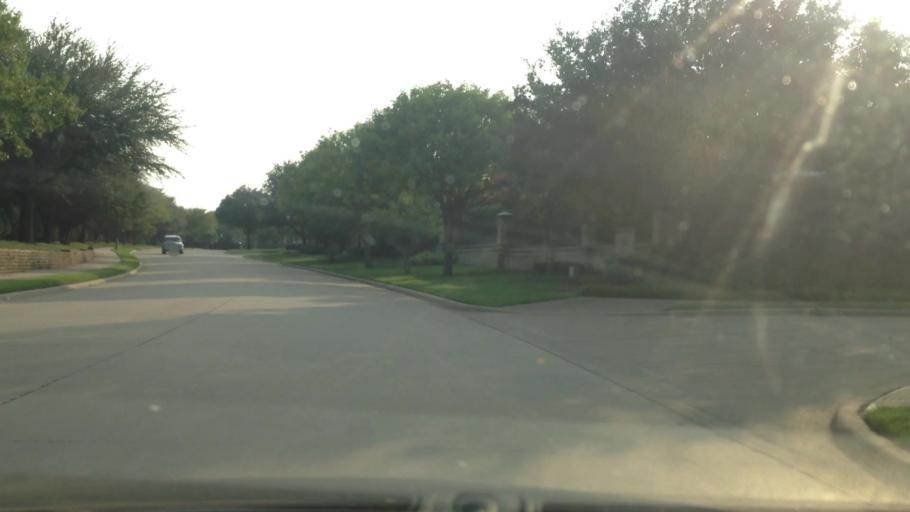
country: US
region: Texas
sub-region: Collin County
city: Frisco
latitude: 33.1198
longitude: -96.8329
